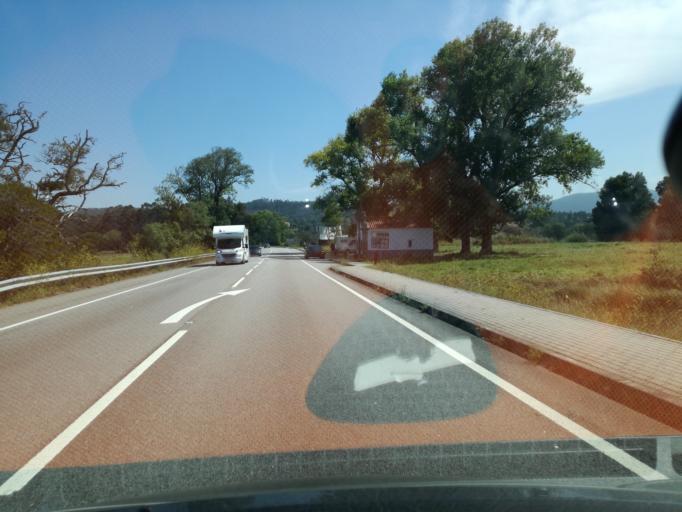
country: ES
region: Galicia
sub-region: Provincia de Pontevedra
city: A Guarda
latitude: 41.8796
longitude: -8.8287
